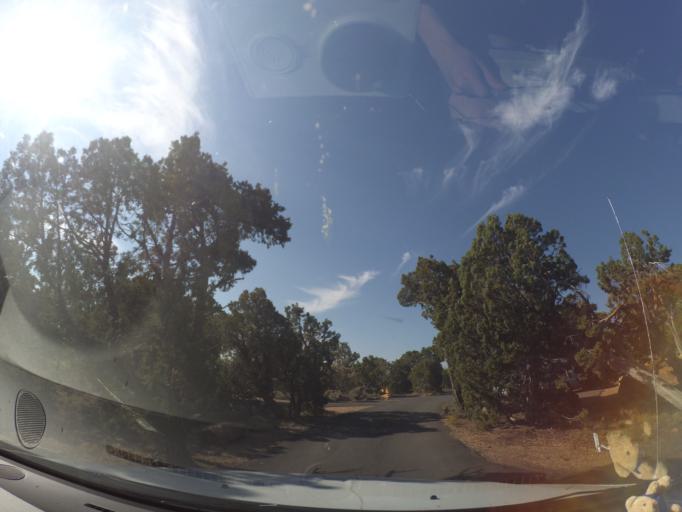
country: US
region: Arizona
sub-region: Coconino County
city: Grand Canyon
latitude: 36.0397
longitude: -111.8224
